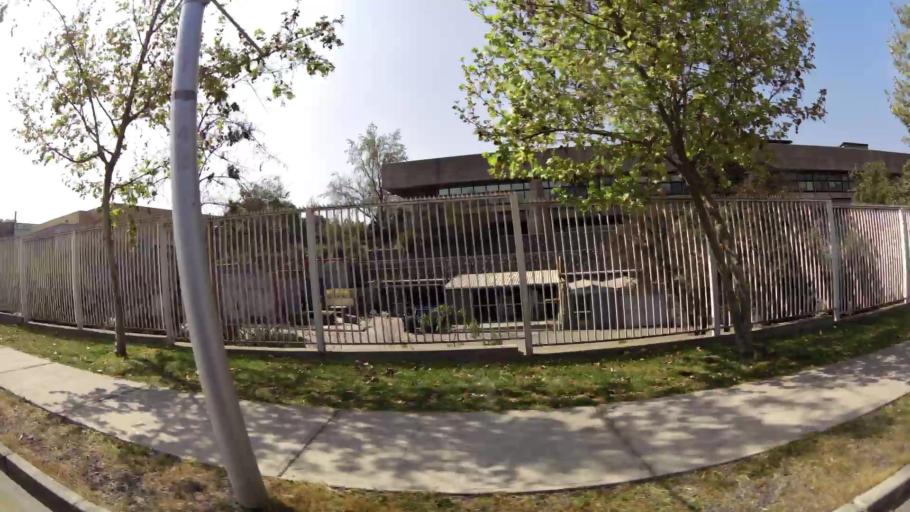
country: CL
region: Santiago Metropolitan
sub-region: Provincia de Santiago
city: Villa Presidente Frei, Nunoa, Santiago, Chile
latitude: -33.4013
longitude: -70.6013
